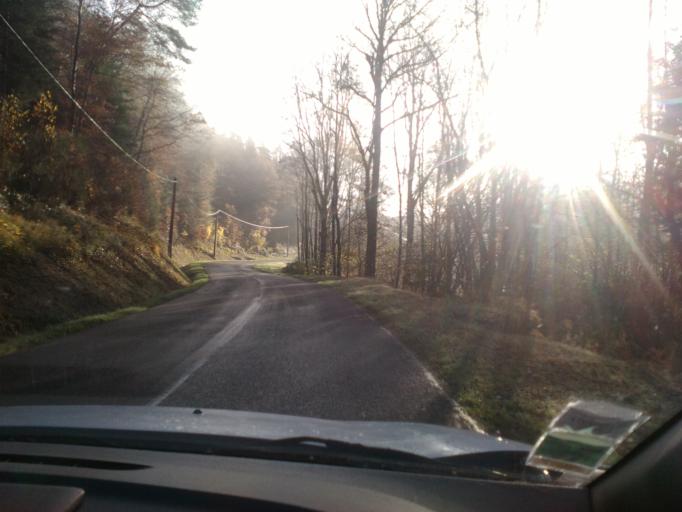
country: FR
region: Lorraine
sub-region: Departement des Vosges
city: Uzemain
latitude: 48.0682
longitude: 6.3167
